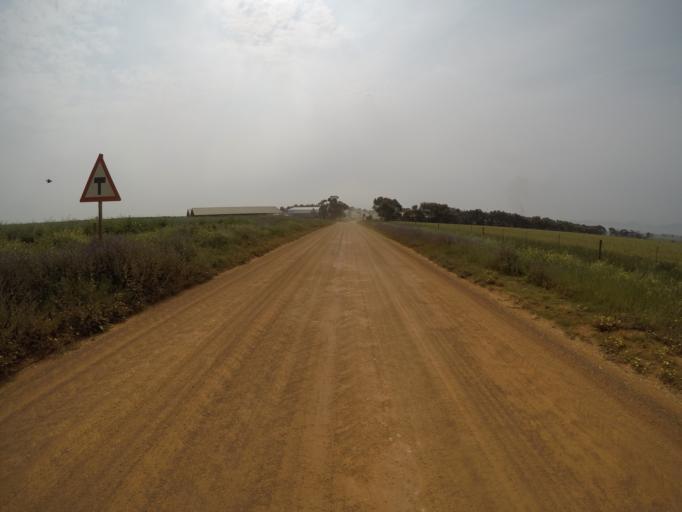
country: ZA
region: Western Cape
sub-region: City of Cape Town
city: Kraaifontein
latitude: -33.7076
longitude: 18.6902
